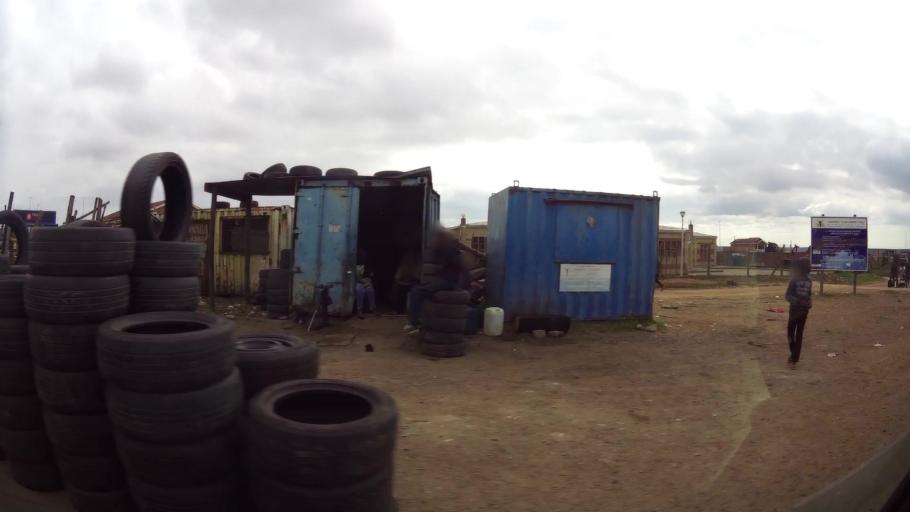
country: ZA
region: Eastern Cape
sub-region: Nelson Mandela Bay Metropolitan Municipality
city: Port Elizabeth
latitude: -33.8691
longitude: 25.5659
